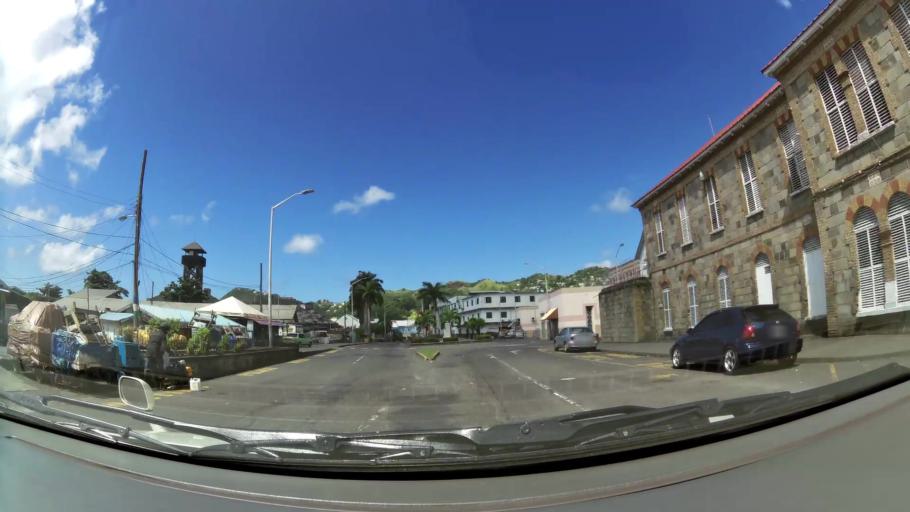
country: VC
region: Saint George
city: Kingstown
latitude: 13.1541
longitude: -61.2255
